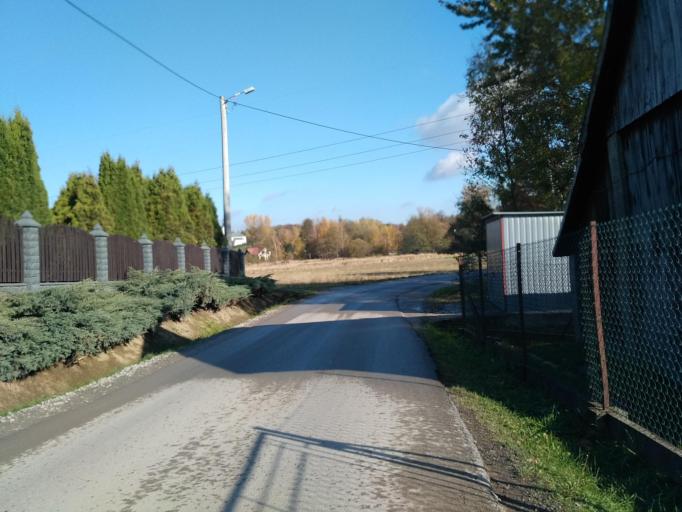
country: PL
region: Subcarpathian Voivodeship
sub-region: Powiat rzeszowski
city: Niechobrz
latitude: 50.0116
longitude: 21.8942
